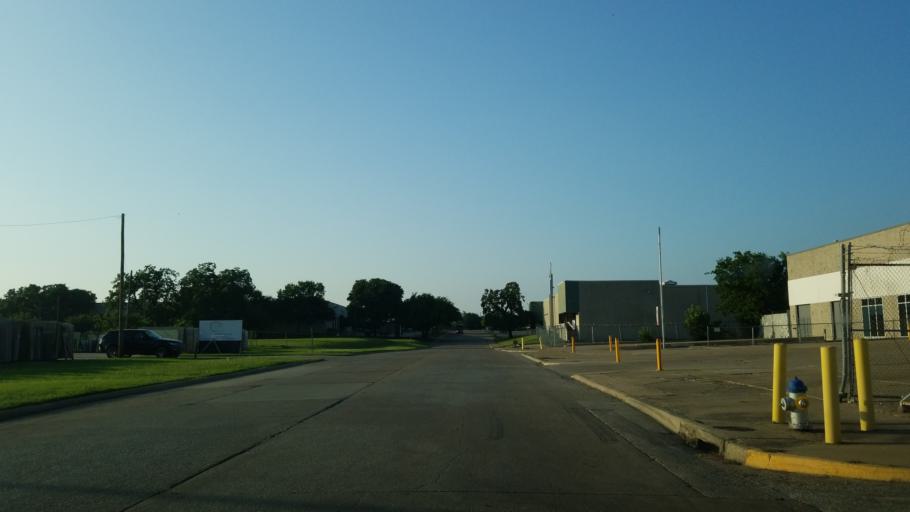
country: US
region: Texas
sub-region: Dallas County
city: Farmers Branch
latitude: 32.8875
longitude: -96.8831
